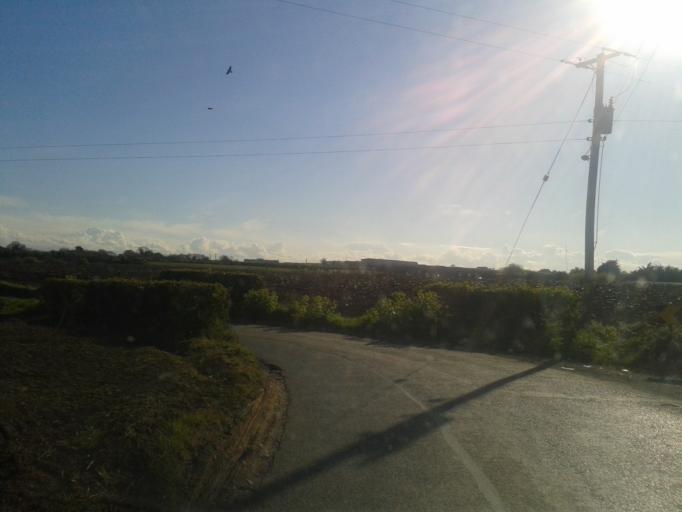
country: IE
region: Leinster
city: Kinsealy-Drinan
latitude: 53.4392
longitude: -6.2122
